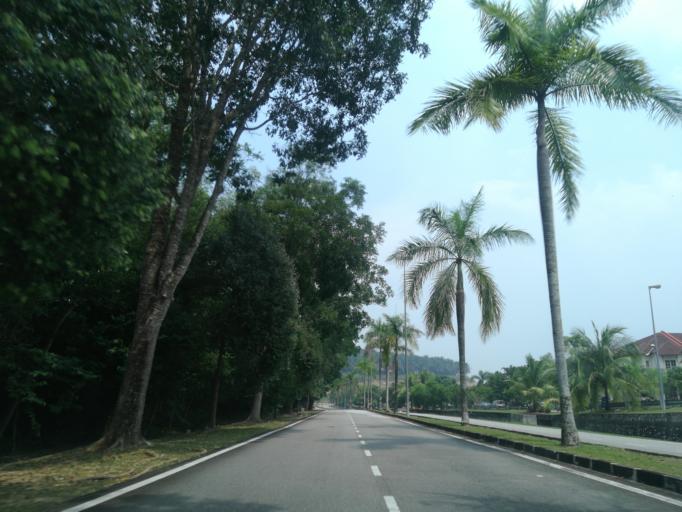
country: MY
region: Kedah
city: Kulim
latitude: 5.3944
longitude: 100.5812
